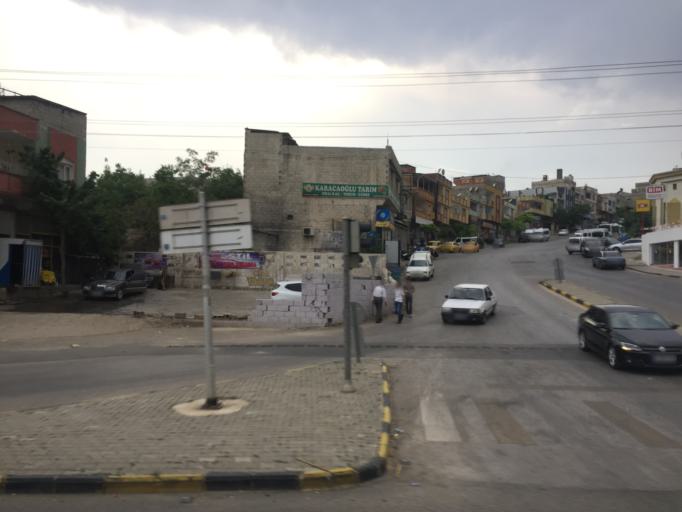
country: TR
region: Gaziantep
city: Gaziantep
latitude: 37.0414
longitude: 37.4241
